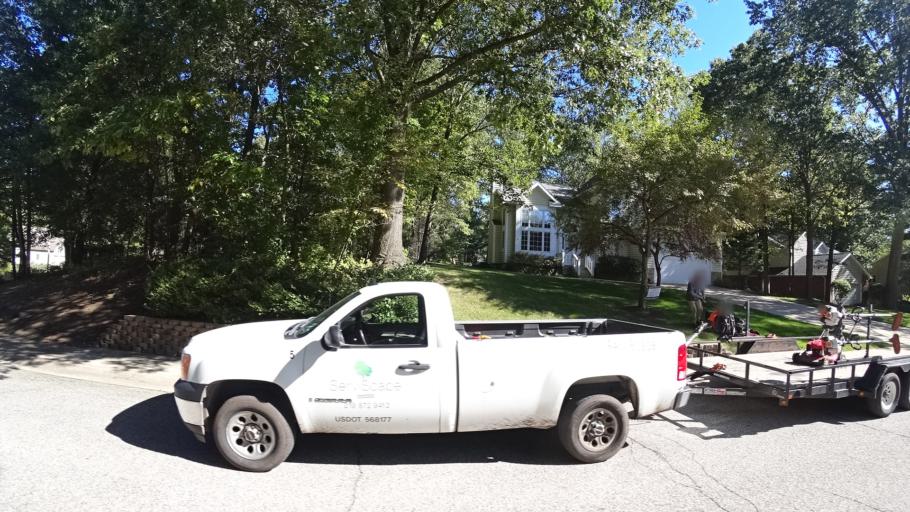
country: US
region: Indiana
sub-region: LaPorte County
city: Long Beach
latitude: 41.7466
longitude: -86.8308
